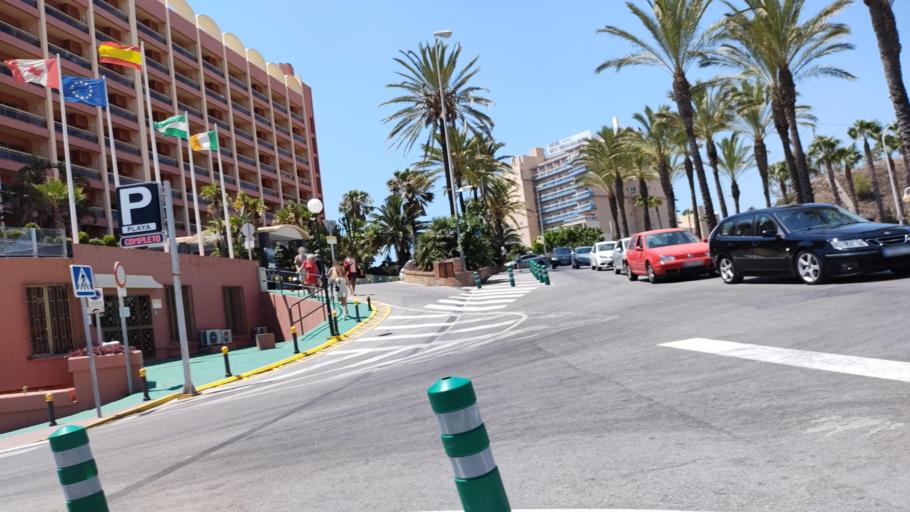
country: ES
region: Andalusia
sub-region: Provincia de Malaga
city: Benalmadena
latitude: 36.5832
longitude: -4.5352
